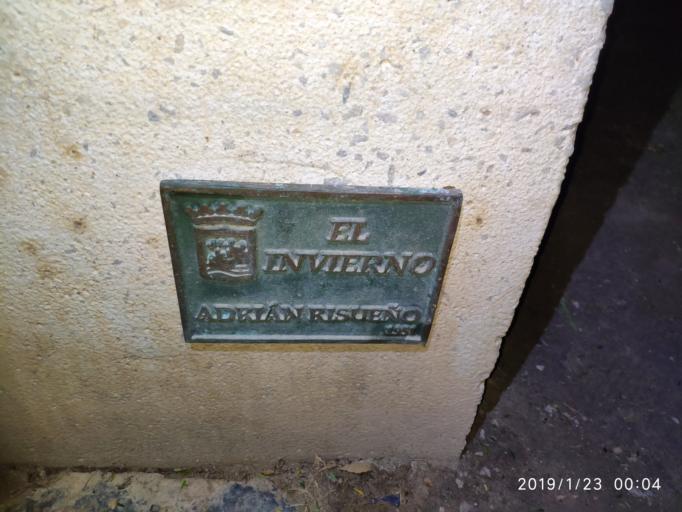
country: ES
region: Andalusia
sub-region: Provincia de Malaga
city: Malaga
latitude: 36.7208
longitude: -4.4173
